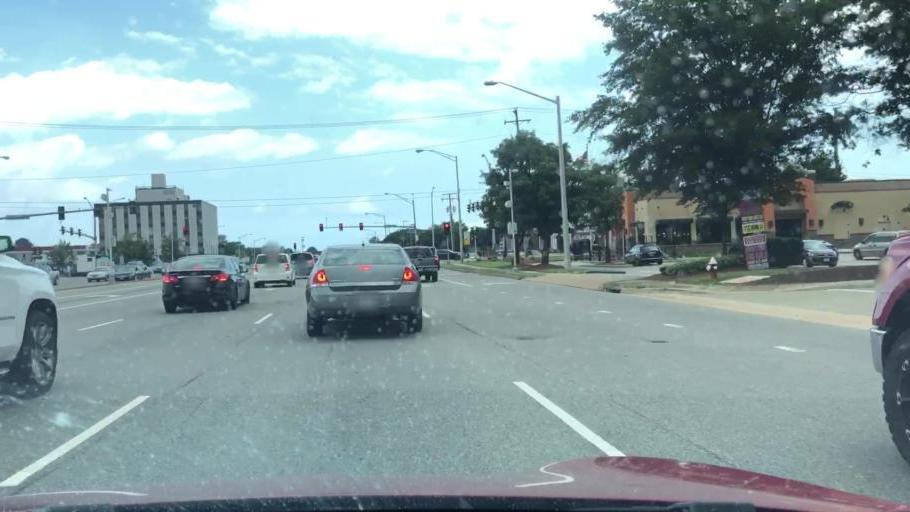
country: US
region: Virginia
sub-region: City of Chesapeake
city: Chesapeake
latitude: 36.8425
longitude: -76.1367
